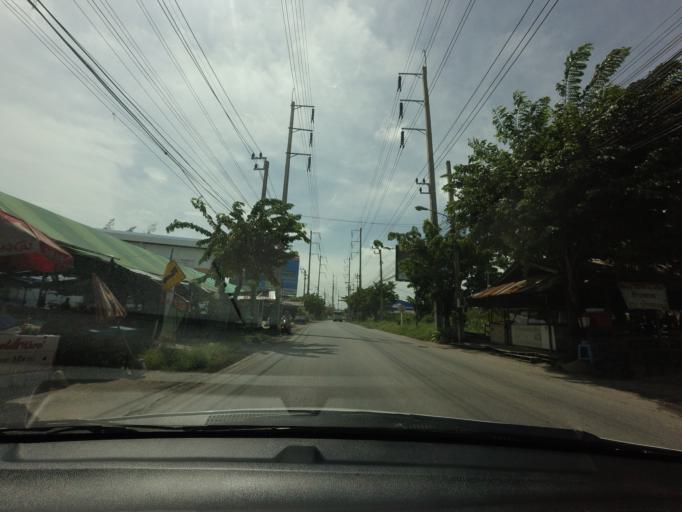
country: TH
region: Bangkok
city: Bang Na
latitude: 13.6160
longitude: 100.6742
